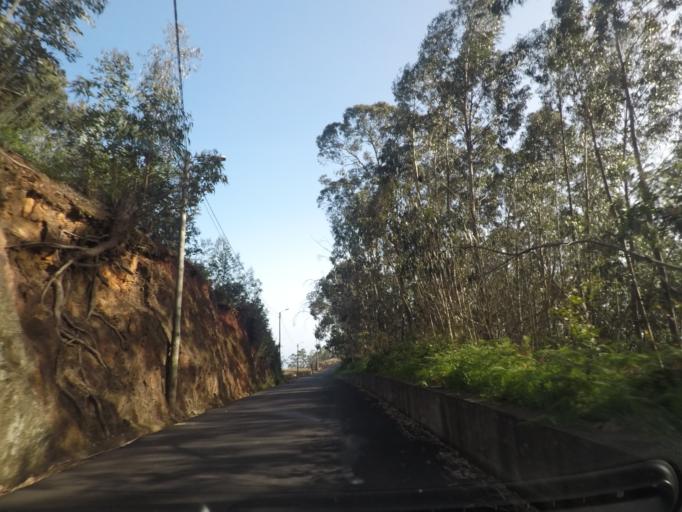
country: PT
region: Madeira
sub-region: Ribeira Brava
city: Campanario
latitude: 32.6703
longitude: -17.0034
